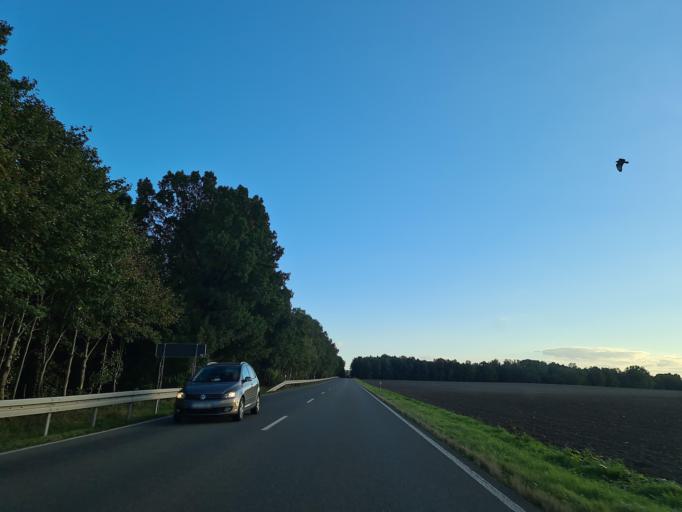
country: DE
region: Thuringia
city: Kuhdorf
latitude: 50.7024
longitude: 12.1167
